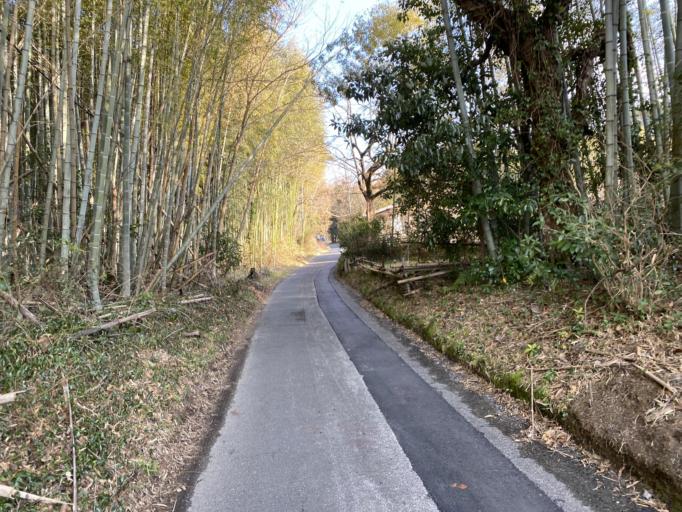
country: JP
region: Nara
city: Nara-shi
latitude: 34.7555
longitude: 135.8805
